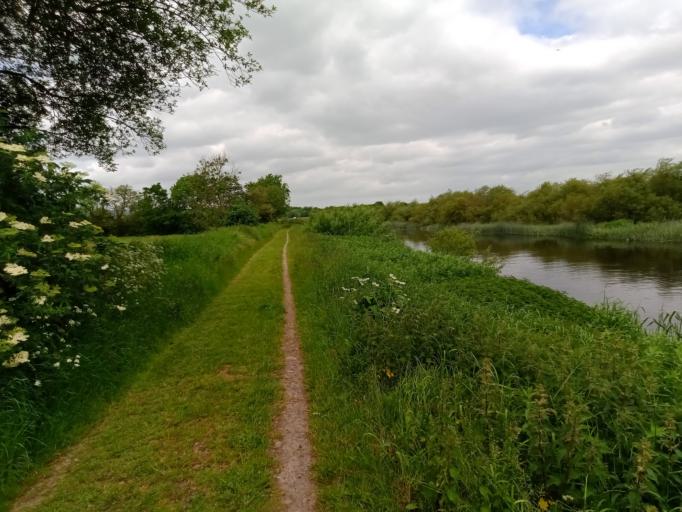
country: IE
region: Leinster
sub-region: County Carlow
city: Bagenalstown
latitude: 52.7605
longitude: -6.9602
